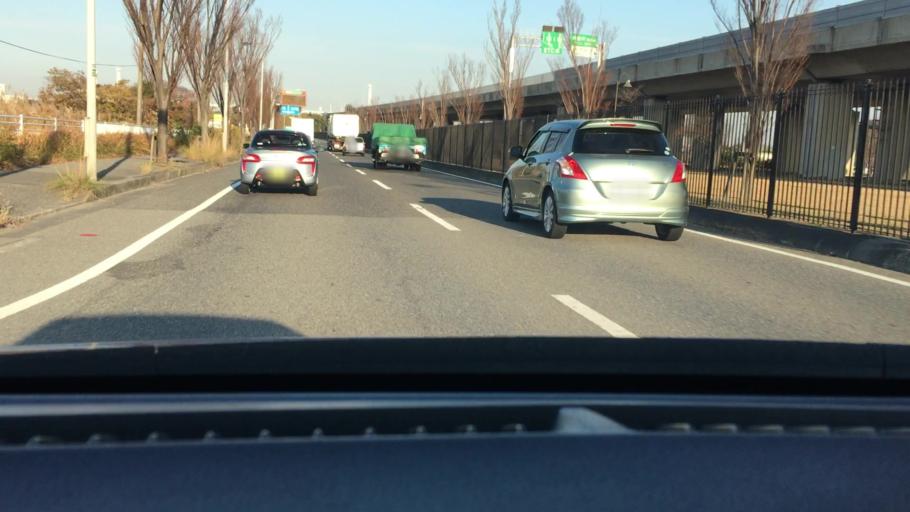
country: JP
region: Chiba
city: Kisarazu
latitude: 35.4317
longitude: 139.9239
